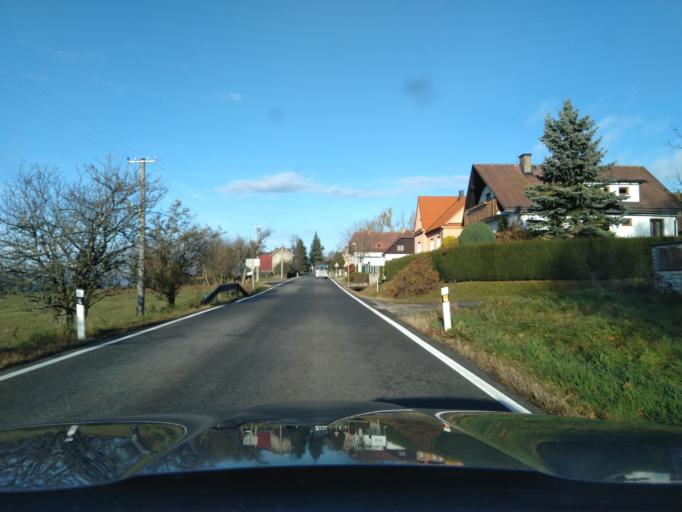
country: CZ
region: Jihocesky
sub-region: Okres Prachatice
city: Stachy
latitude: 49.1229
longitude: 13.6222
